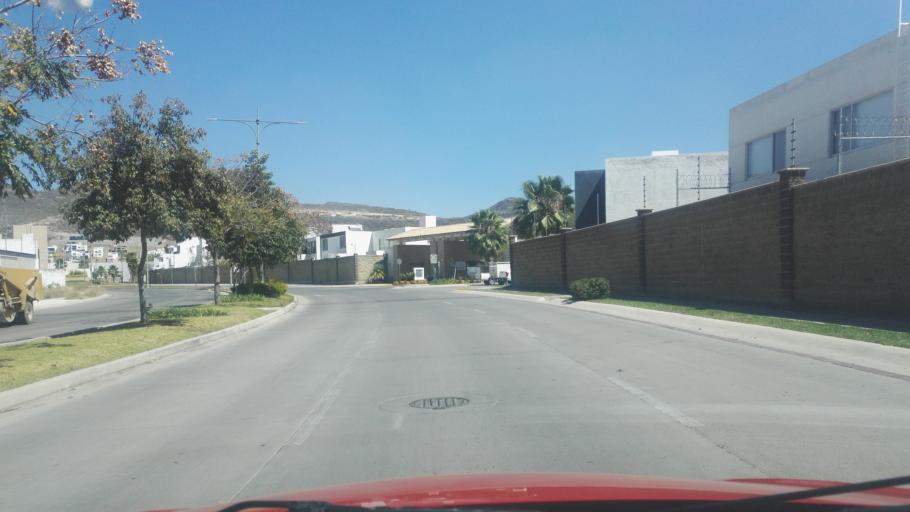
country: MX
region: Guanajuato
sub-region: Leon
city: Medina
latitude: 21.1284
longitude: -101.6065
